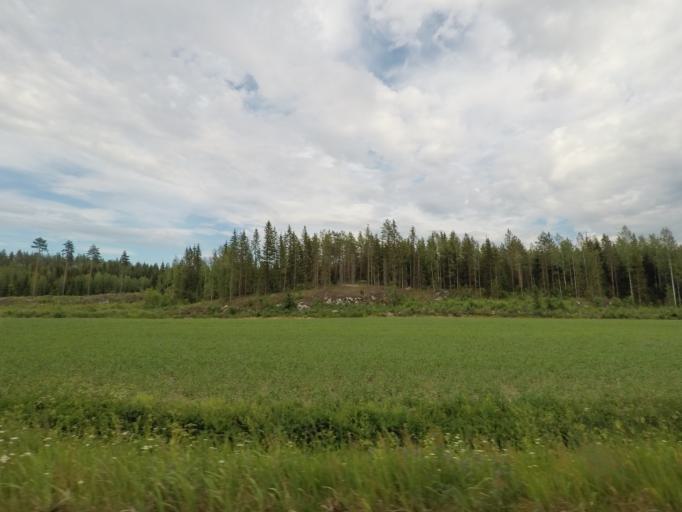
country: FI
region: Paijanne Tavastia
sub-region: Lahti
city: Hollola
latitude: 60.8378
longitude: 25.4932
